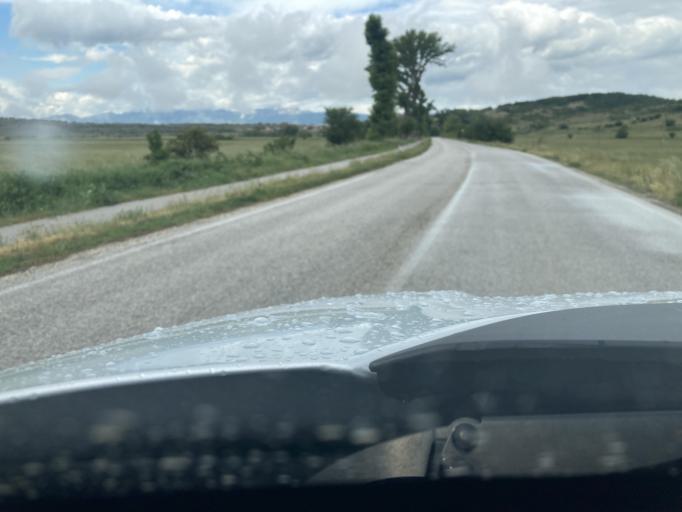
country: IT
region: Abruzzo
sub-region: Provincia dell' Aquila
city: Rocca di Mezzo
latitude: 42.2170
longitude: 13.5304
